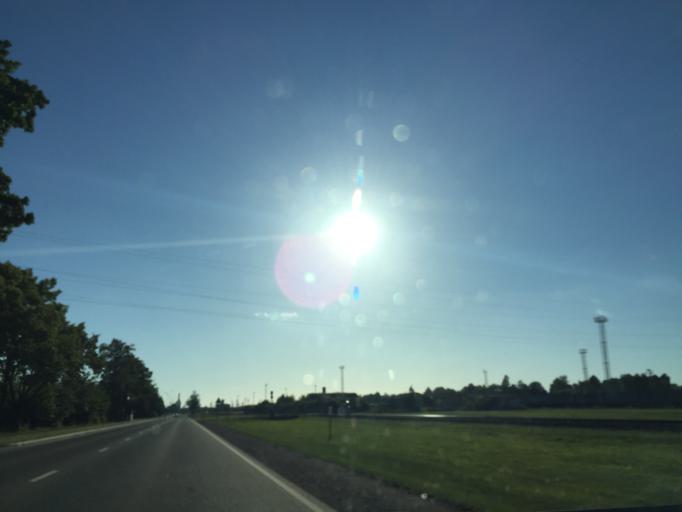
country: LV
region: Ventspils
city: Ventspils
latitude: 57.3944
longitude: 21.6274
